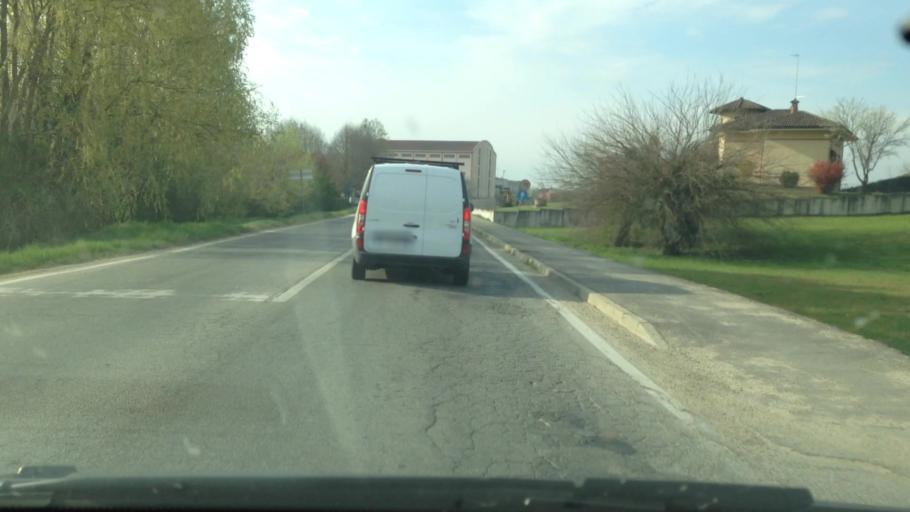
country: IT
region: Piedmont
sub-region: Provincia di Asti
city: San Damiano d'Asti
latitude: 44.8318
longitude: 8.0600
